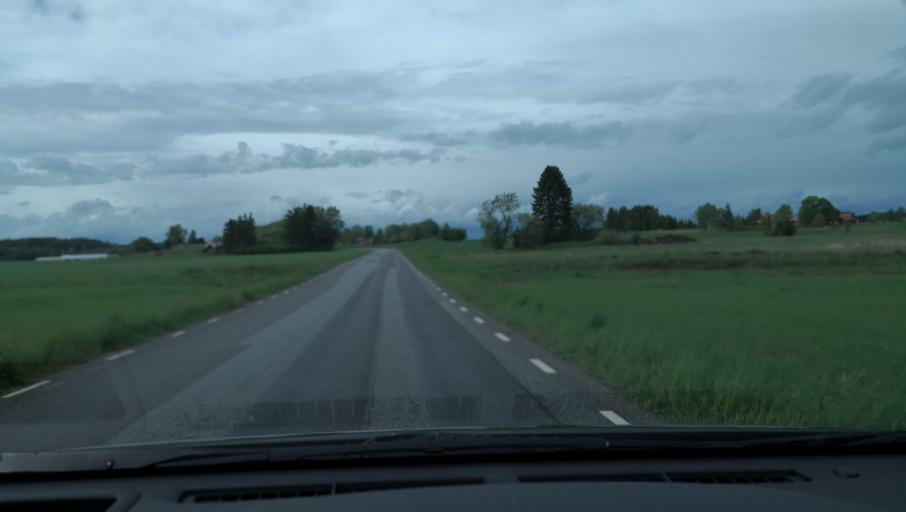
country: SE
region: Uppsala
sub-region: Enkopings Kommun
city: Orsundsbro
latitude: 59.6964
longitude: 17.3694
